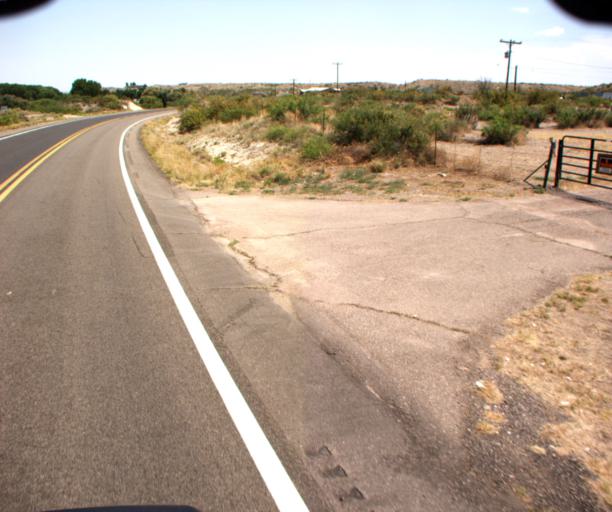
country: US
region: Arizona
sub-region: Greenlee County
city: Clifton
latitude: 32.7408
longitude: -109.1275
